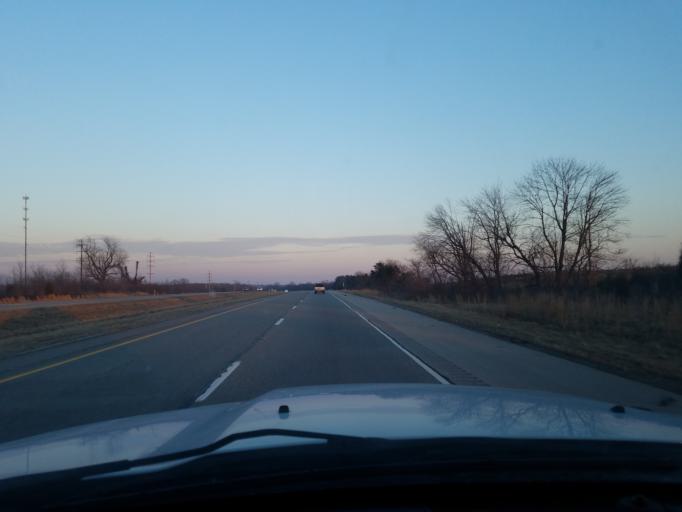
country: US
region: Indiana
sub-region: Warrick County
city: Boonville
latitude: 38.1994
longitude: -87.2668
